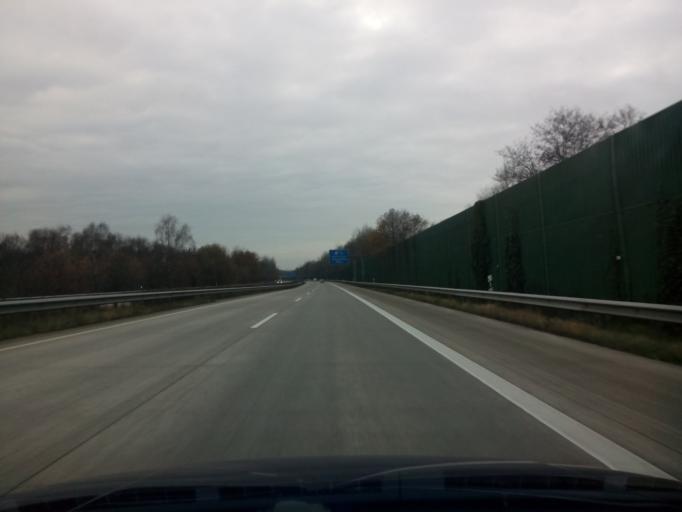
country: DE
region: Lower Saxony
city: Langen
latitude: 53.5903
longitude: 8.6344
